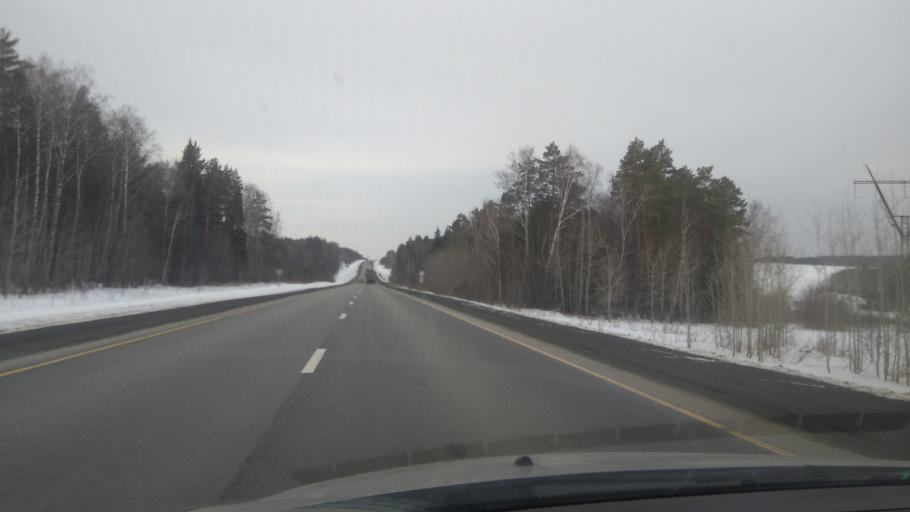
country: RU
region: Sverdlovsk
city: Bisert'
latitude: 56.8234
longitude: 58.7637
